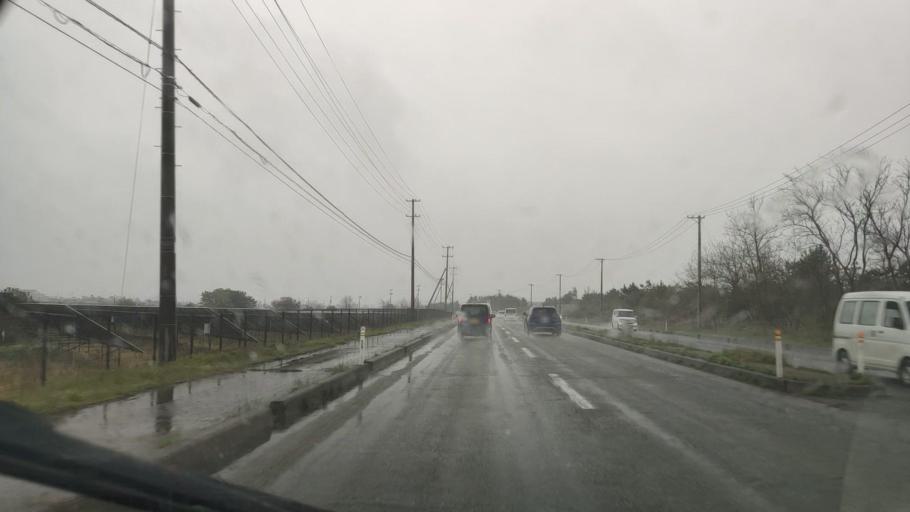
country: JP
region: Akita
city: Tenno
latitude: 39.8871
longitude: 139.9676
